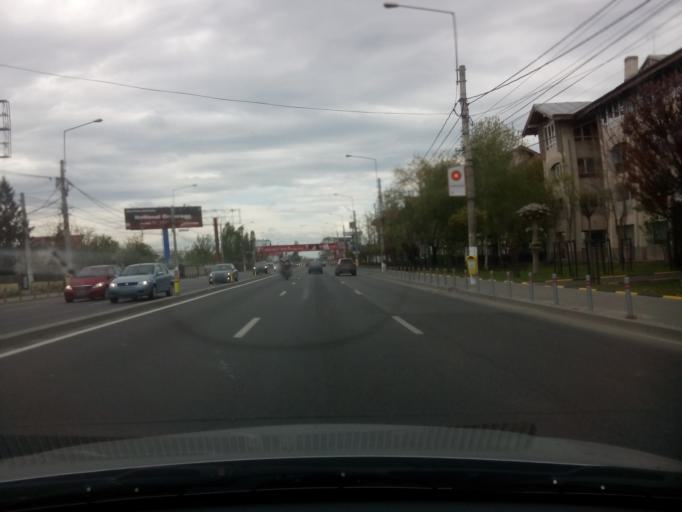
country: RO
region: Ilfov
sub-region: Comuna Otopeni
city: Otopeni
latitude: 44.5526
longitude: 26.0691
